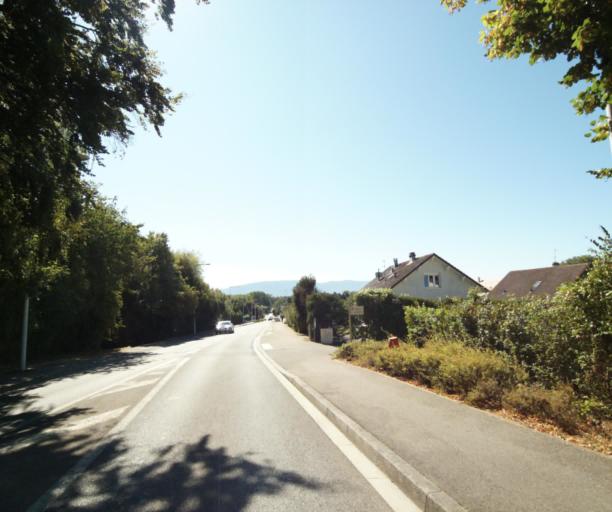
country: FR
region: Rhone-Alpes
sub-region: Departement de l'Ain
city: Ornex
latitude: 46.2664
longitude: 6.1007
